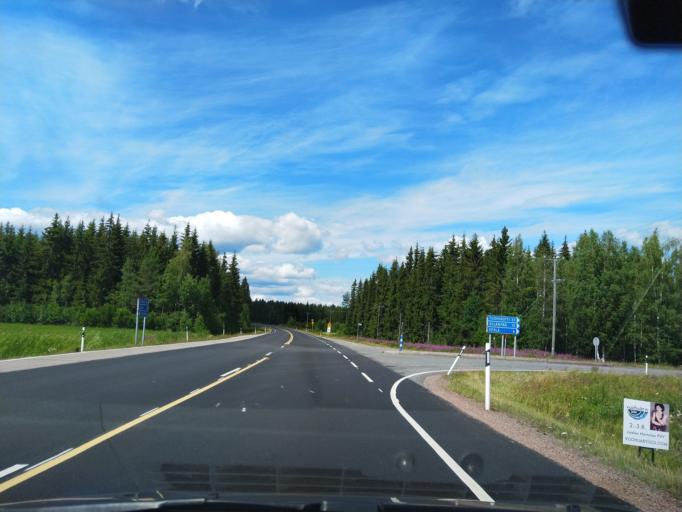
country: FI
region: Kymenlaakso
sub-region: Kouvola
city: Jaala
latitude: 61.0403
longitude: 26.5545
